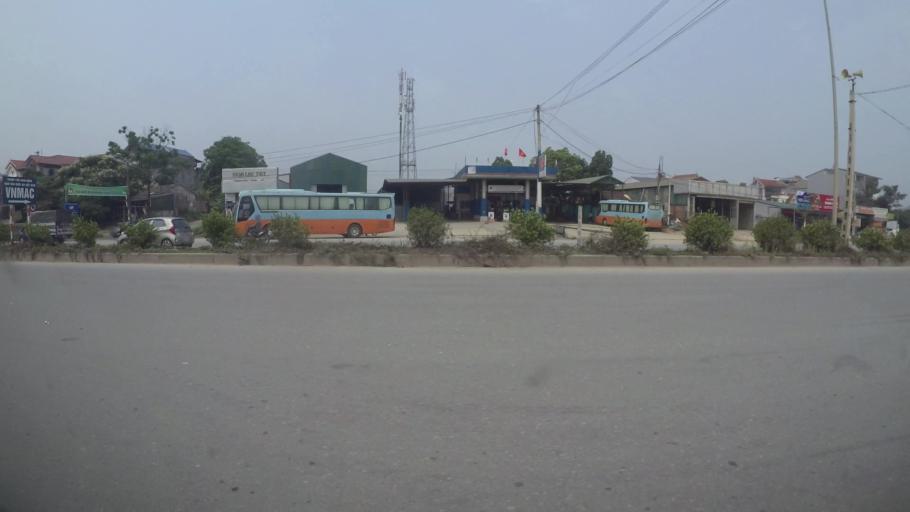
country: VN
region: Ha Noi
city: Lien Quan
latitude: 20.9861
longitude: 105.5258
